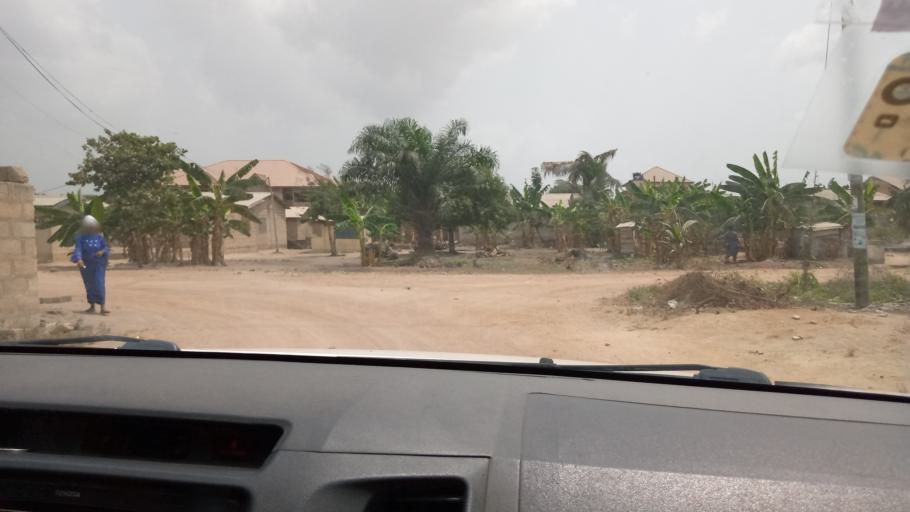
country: GH
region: Central
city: Kasoa
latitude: 5.5338
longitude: -0.4502
